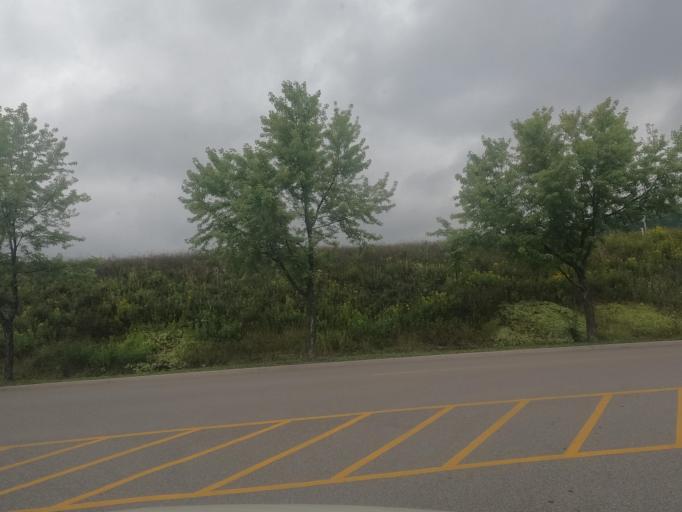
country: CA
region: Ontario
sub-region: Algoma
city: Sault Ste. Marie
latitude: 46.5137
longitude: -84.3493
